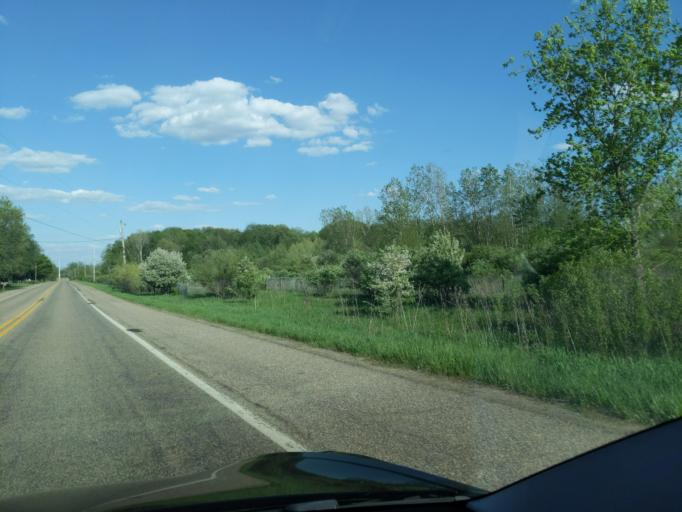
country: US
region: Michigan
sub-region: Eaton County
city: Dimondale
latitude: 42.6829
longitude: -84.6755
